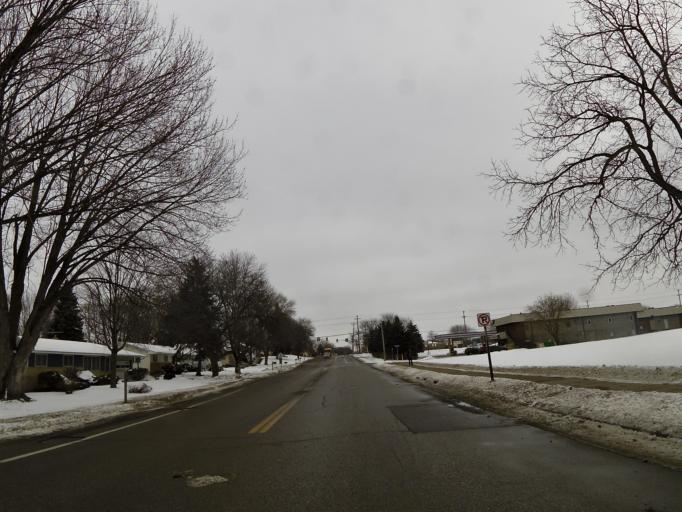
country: US
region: Minnesota
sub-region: Ramsey County
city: North Saint Paul
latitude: 45.0067
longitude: -92.9872
